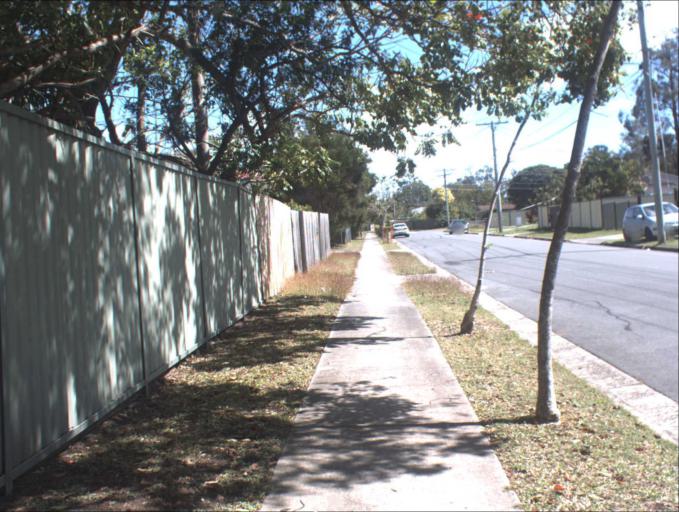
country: AU
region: Queensland
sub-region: Logan
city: Waterford West
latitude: -27.6738
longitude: 153.1092
